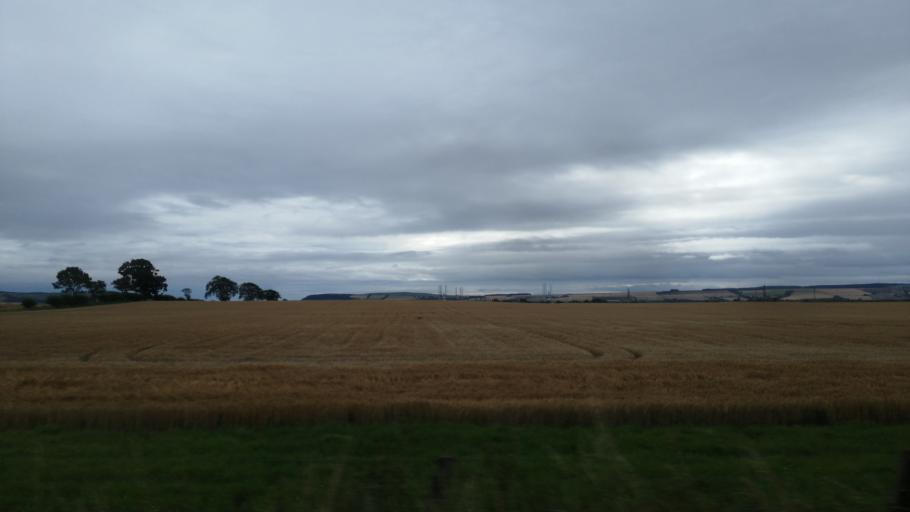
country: GB
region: Scotland
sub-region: Highland
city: Invergordon
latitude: 57.7174
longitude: -4.1219
